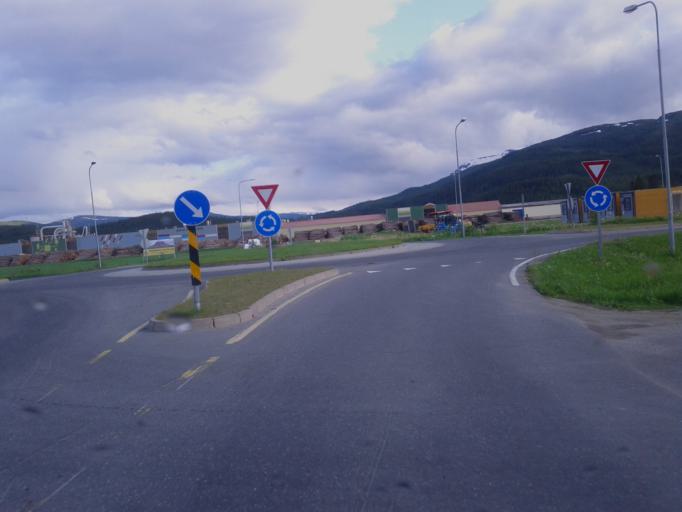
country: NO
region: Nordland
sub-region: Hattfjelldal
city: Hattfjelldal
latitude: 65.5966
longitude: 13.9909
